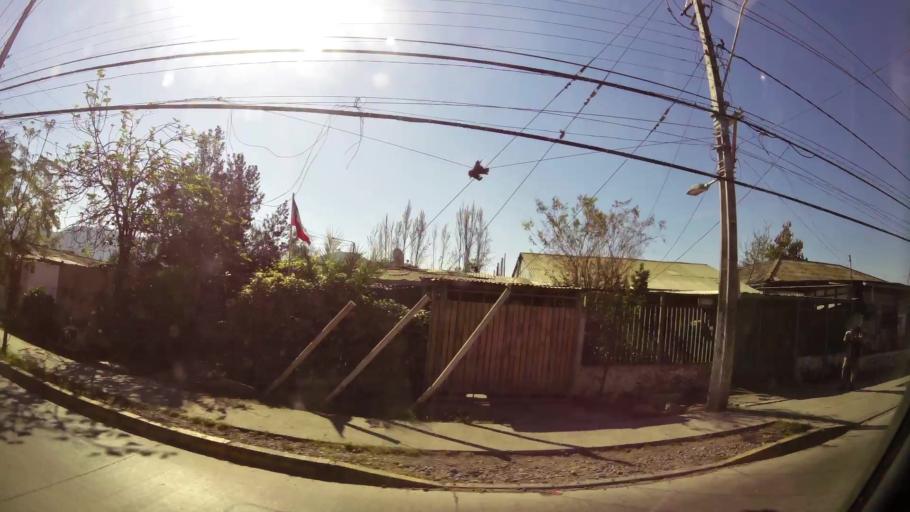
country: CL
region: Santiago Metropolitan
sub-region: Provincia de Talagante
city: Penaflor
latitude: -33.6060
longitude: -70.8923
